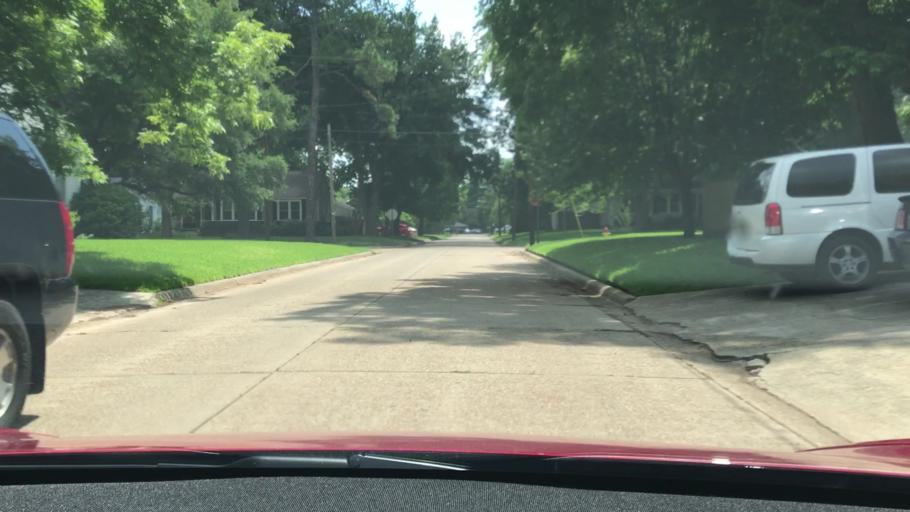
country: US
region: Louisiana
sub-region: Bossier Parish
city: Bossier City
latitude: 32.4579
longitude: -93.7254
